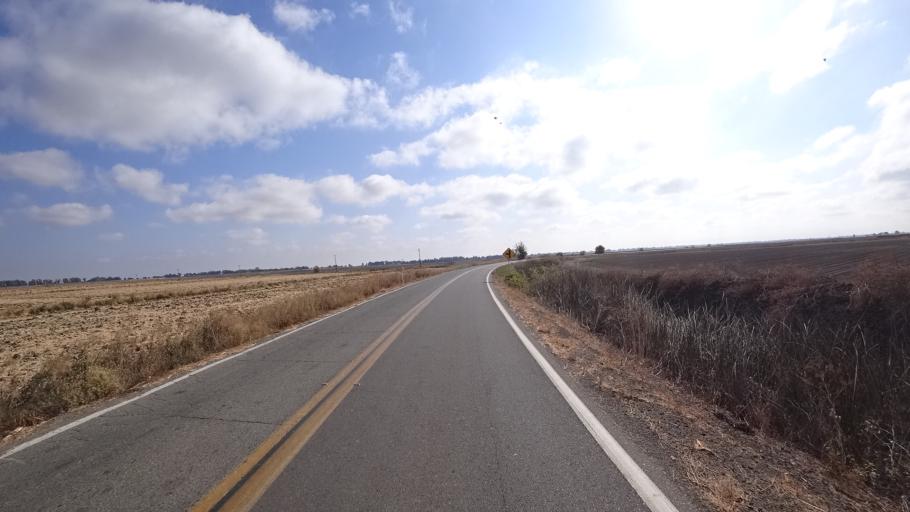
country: US
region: California
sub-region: Yolo County
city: Woodland
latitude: 38.8456
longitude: -121.7548
